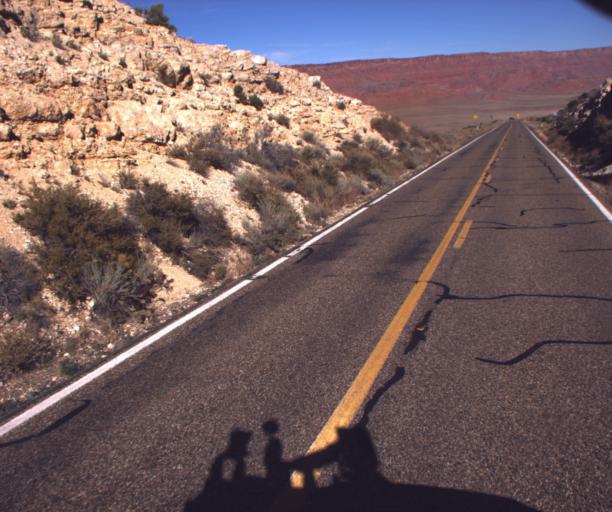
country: US
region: Arizona
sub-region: Coconino County
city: Fredonia
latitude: 36.7254
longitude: -112.0711
